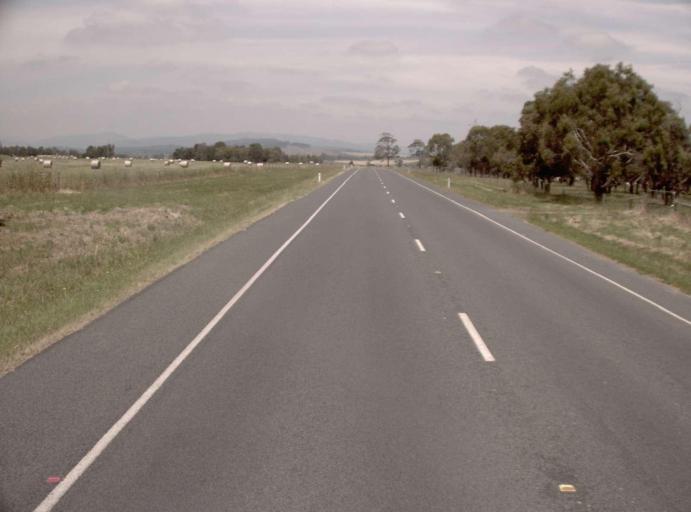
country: AU
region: Victoria
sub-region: Latrobe
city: Traralgon
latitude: -38.2252
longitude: 146.5433
